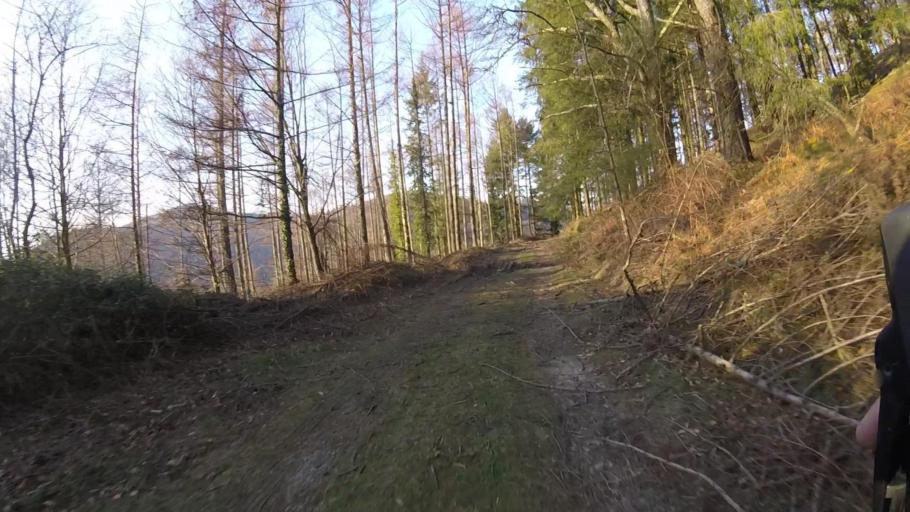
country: ES
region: Navarre
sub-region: Provincia de Navarra
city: Arano
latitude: 43.2455
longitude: -1.8620
